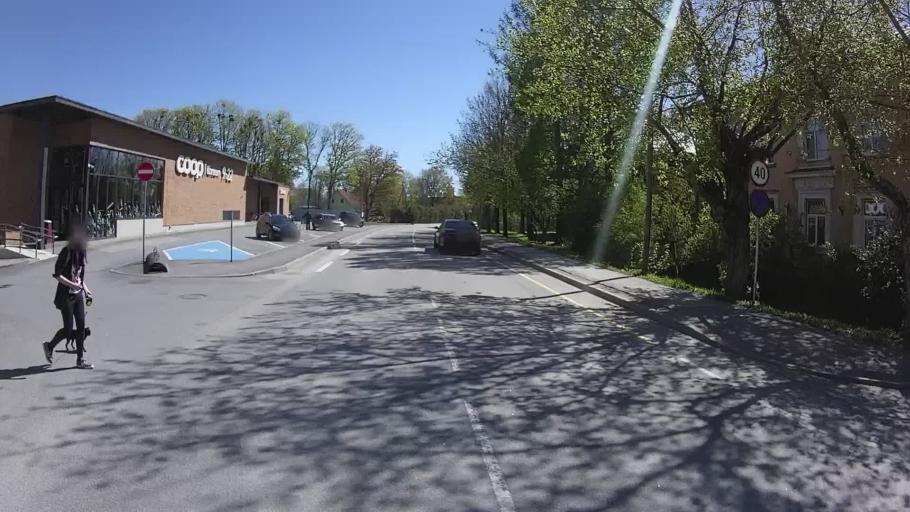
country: EE
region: Harju
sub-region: Raasiku vald
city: Raasiku
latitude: 59.1848
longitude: 25.1666
